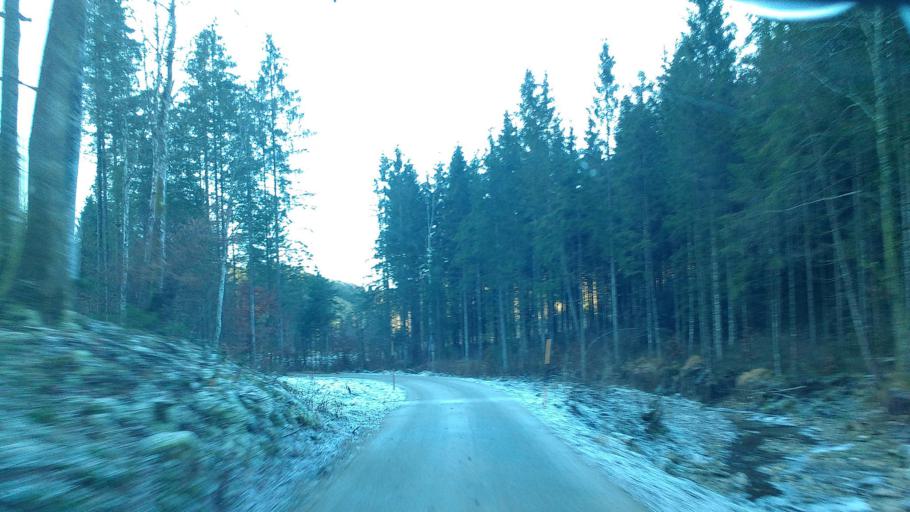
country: AT
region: Upper Austria
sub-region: Politischer Bezirk Kirchdorf an der Krems
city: Micheldorf in Oberoesterreich
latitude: 47.9012
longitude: 14.1825
